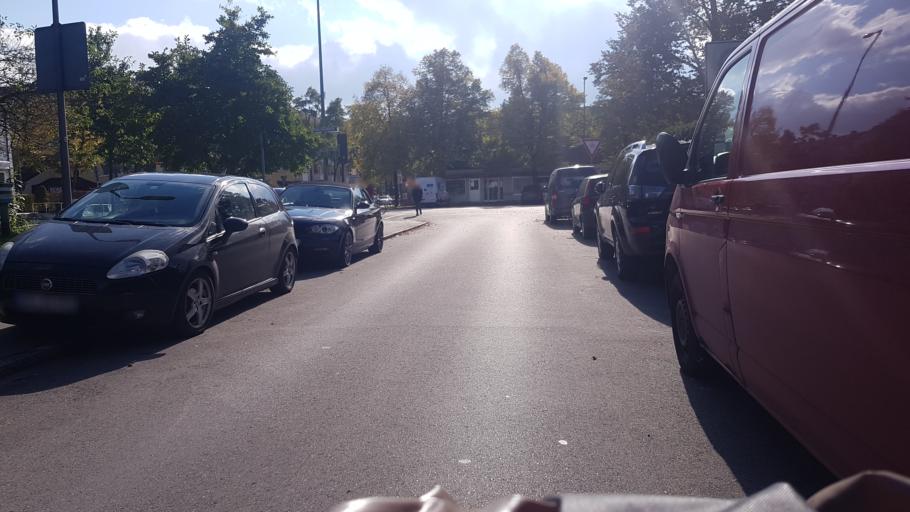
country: DE
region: Bavaria
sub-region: Upper Bavaria
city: Pasing
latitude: 48.1305
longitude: 11.4894
